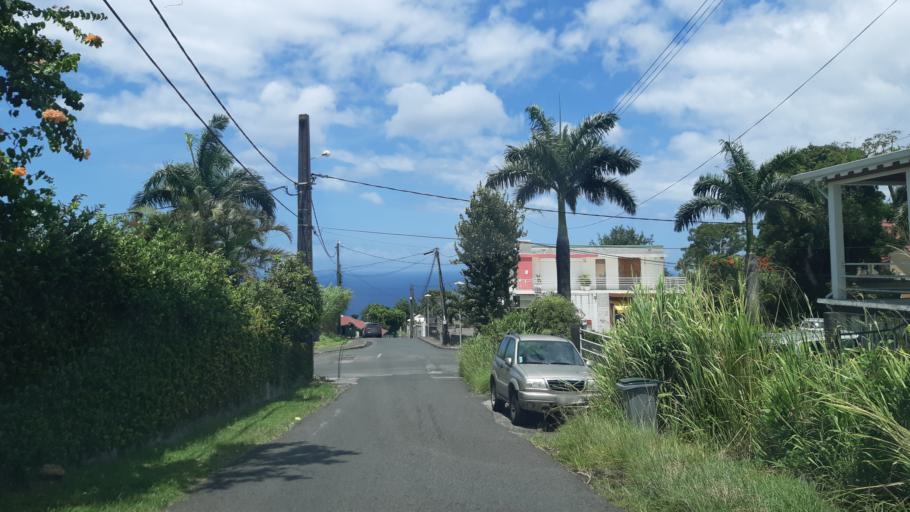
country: GP
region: Guadeloupe
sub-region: Guadeloupe
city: Saint-Claude
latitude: 16.0121
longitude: -61.7111
